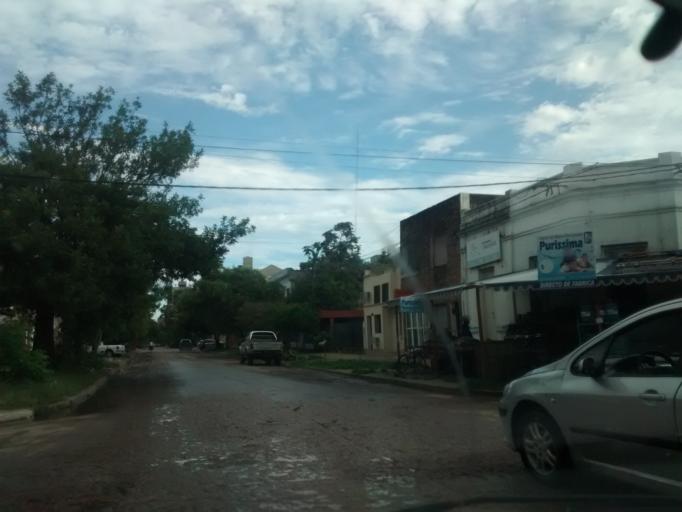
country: AR
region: Chaco
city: Resistencia
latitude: -27.4457
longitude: -58.9944
